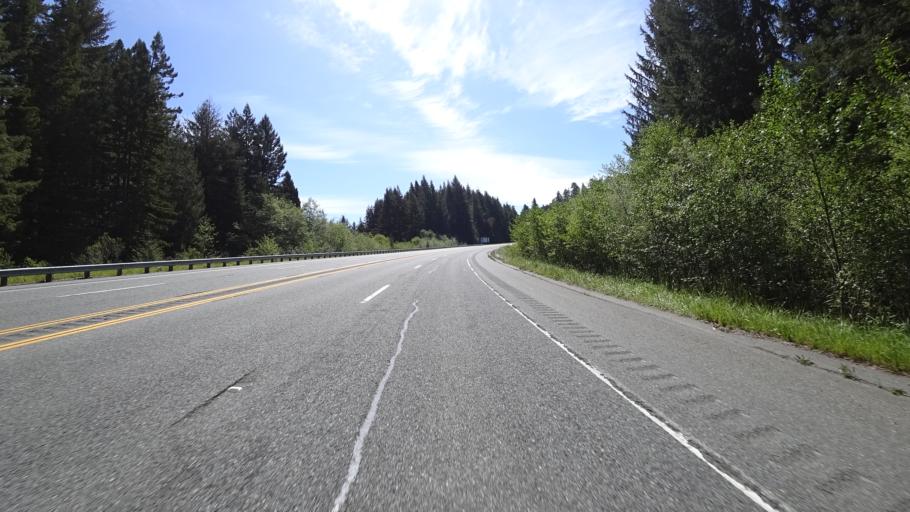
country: US
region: California
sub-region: Del Norte County
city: Bertsch-Oceanview
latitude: 41.4522
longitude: -124.0273
